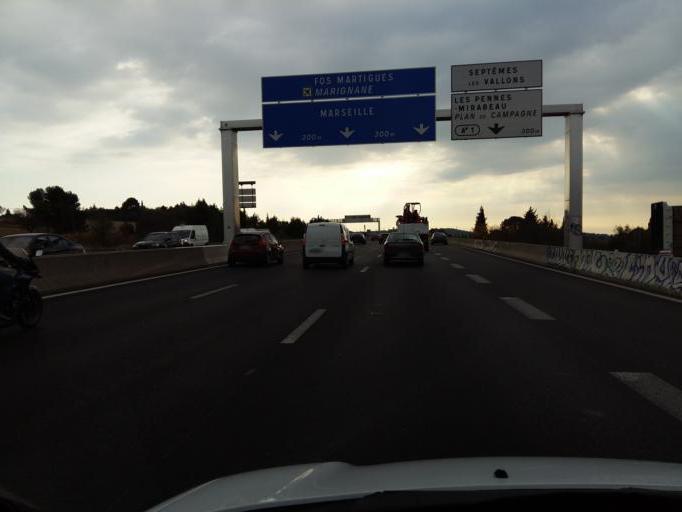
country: FR
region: Provence-Alpes-Cote d'Azur
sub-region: Departement des Bouches-du-Rhone
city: Cabries
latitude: 43.4243
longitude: 5.3750
